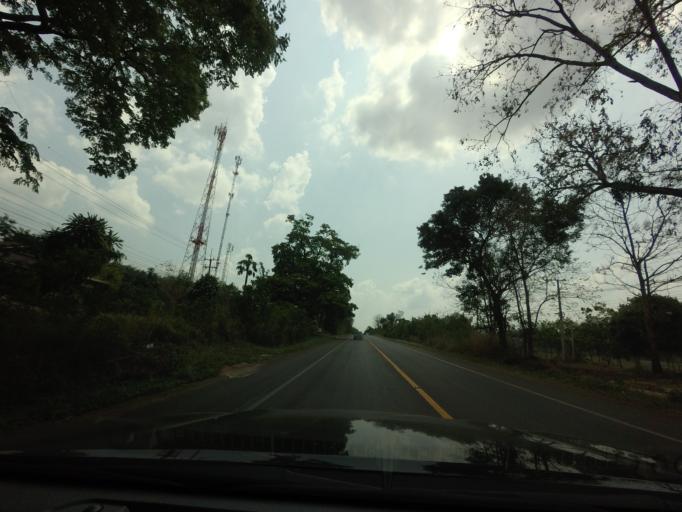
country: TH
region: Kanchanaburi
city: Sai Yok
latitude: 14.1561
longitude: 99.1397
